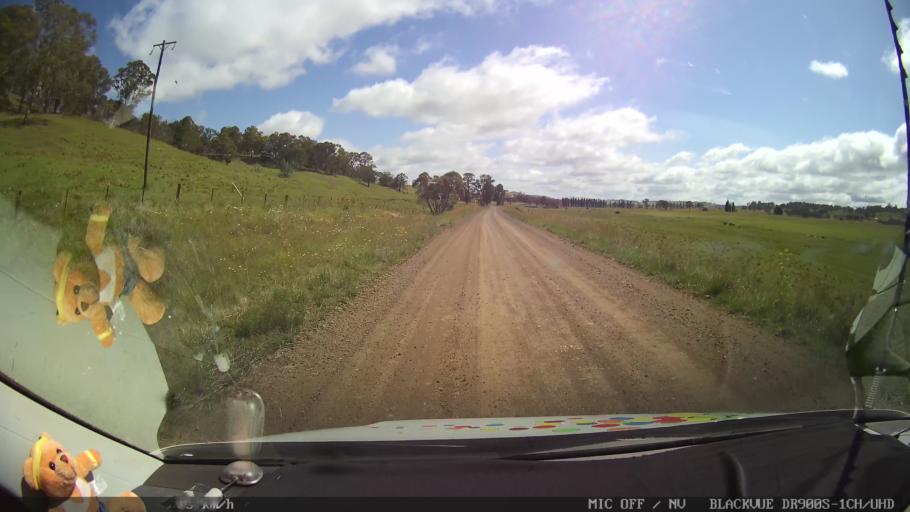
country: AU
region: New South Wales
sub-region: Glen Innes Severn
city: Glen Innes
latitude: -29.9540
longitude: 151.7048
